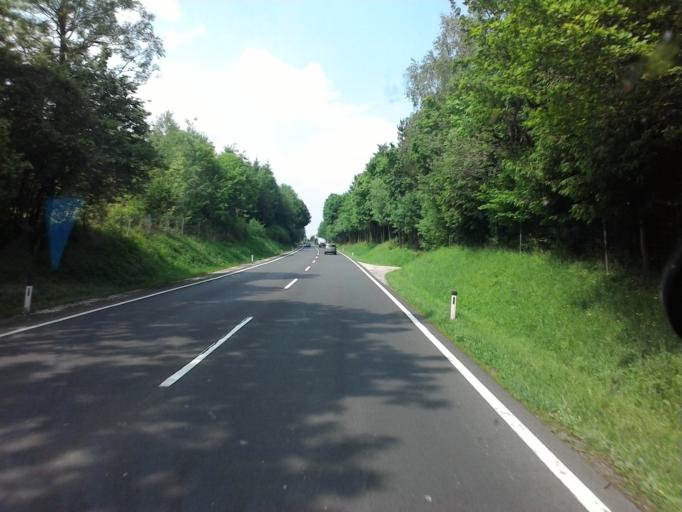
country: AT
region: Upper Austria
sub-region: Wels-Land
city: Steinhaus
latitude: 48.0979
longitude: 14.0410
